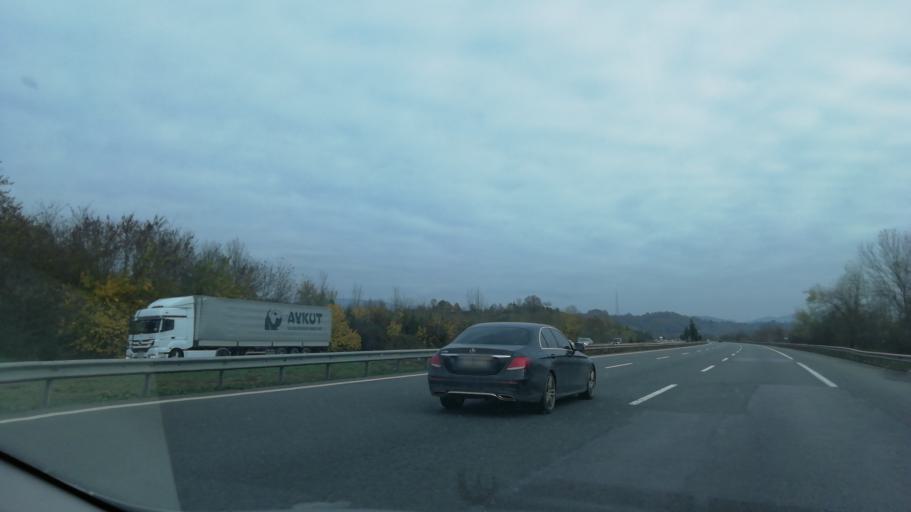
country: TR
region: Sakarya
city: Hendek
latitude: 40.7592
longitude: 30.7504
